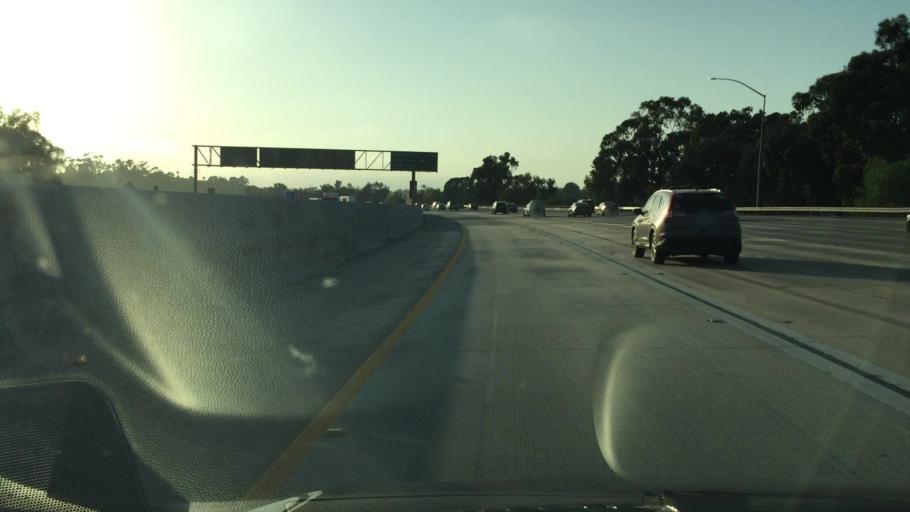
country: US
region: California
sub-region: San Diego County
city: Chula Vista
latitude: 32.6468
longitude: -117.0597
